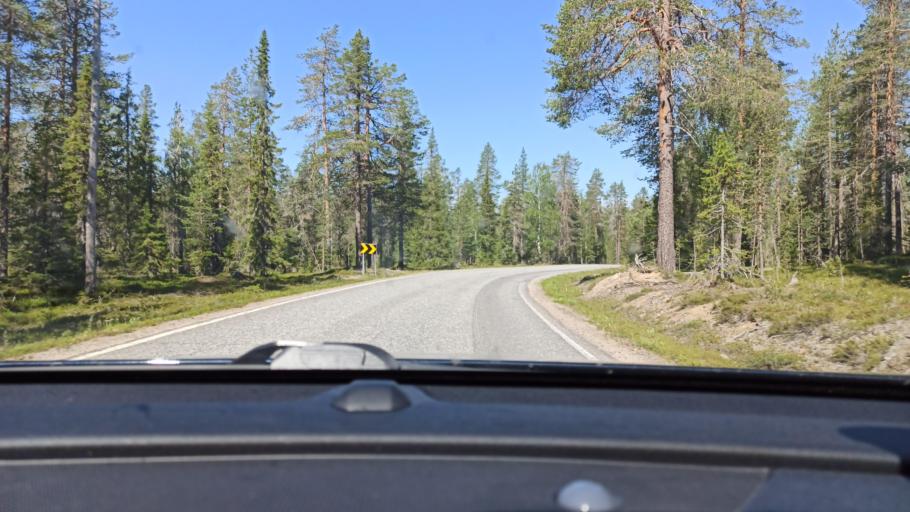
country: FI
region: Lapland
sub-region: Tunturi-Lappi
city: Kolari
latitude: 67.6706
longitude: 24.1510
